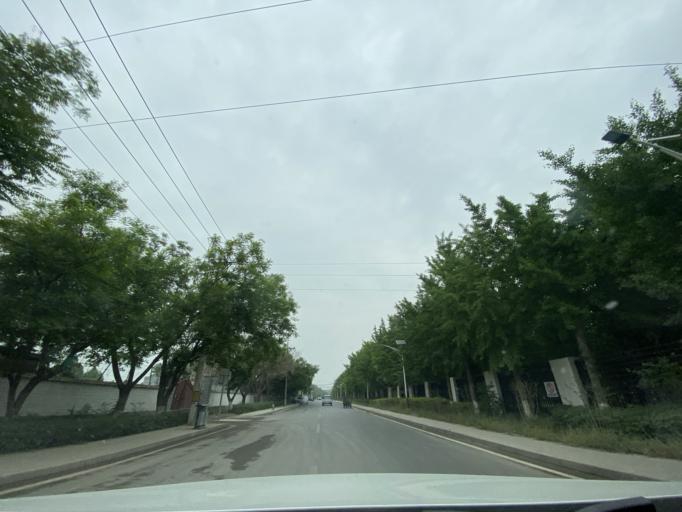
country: CN
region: Beijing
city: Sijiqing
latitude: 39.9338
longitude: 116.2390
